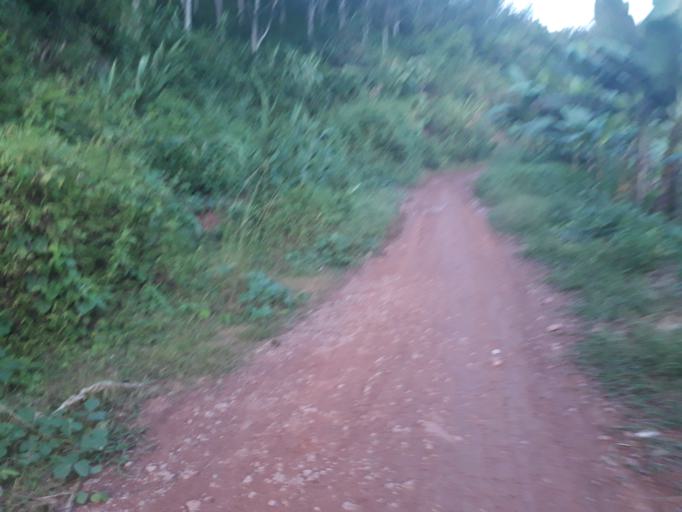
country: CN
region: Yunnan
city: Menglie
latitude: 22.1216
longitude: 101.7724
